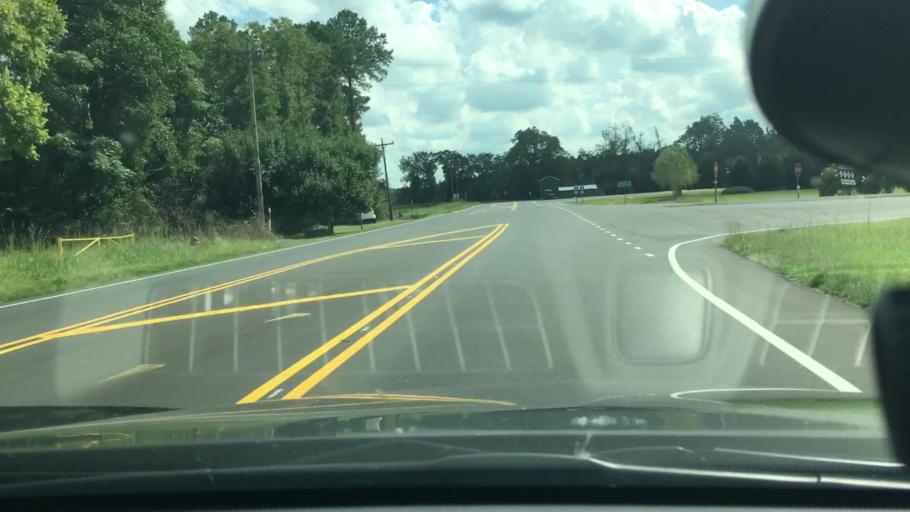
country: US
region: North Carolina
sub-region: Edgecombe County
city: Pinetops
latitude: 35.7790
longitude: -77.5851
